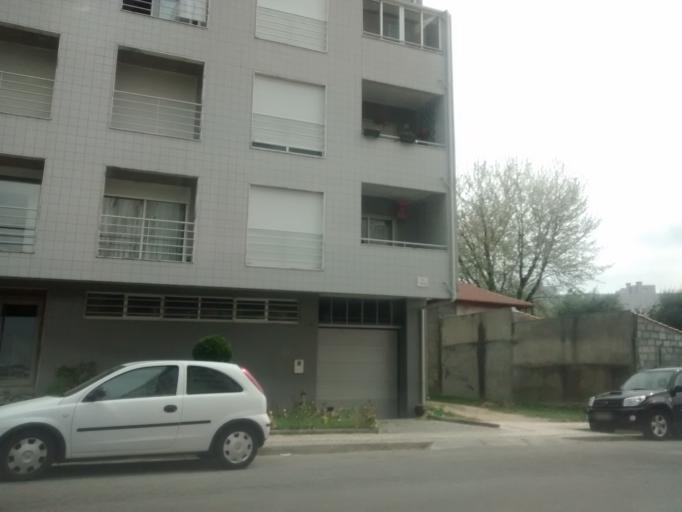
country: PT
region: Braga
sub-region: Braga
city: Braga
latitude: 41.5588
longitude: -8.4038
